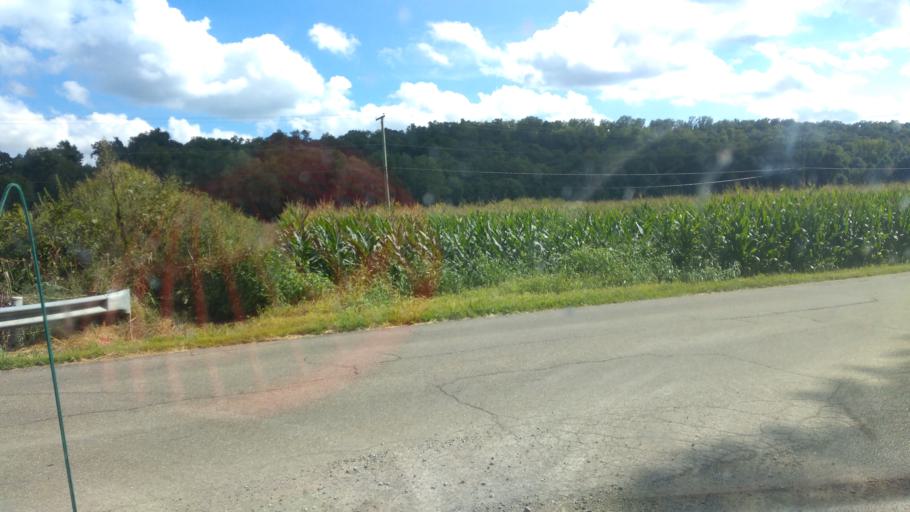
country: US
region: Ohio
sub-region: Holmes County
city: Millersburg
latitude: 40.6431
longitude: -81.8940
